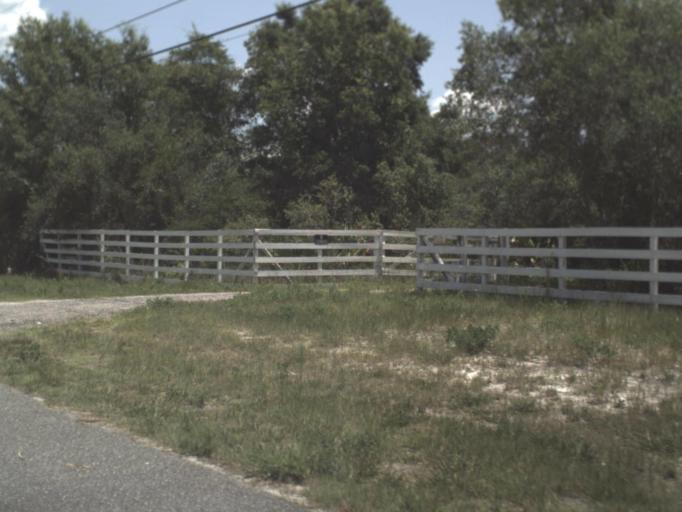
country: US
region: Florida
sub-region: Taylor County
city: Steinhatchee
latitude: 29.6967
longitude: -83.3568
